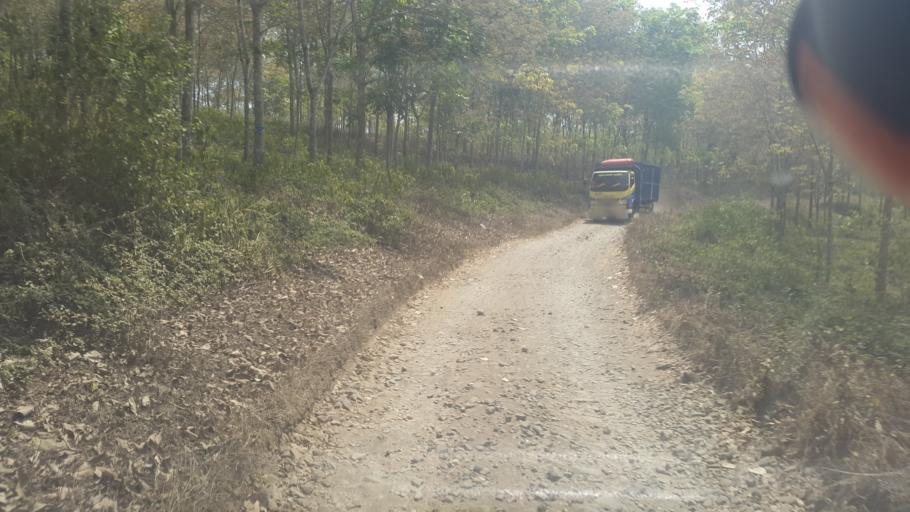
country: ID
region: West Java
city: Ciroyom
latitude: -7.0959
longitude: 106.8597
